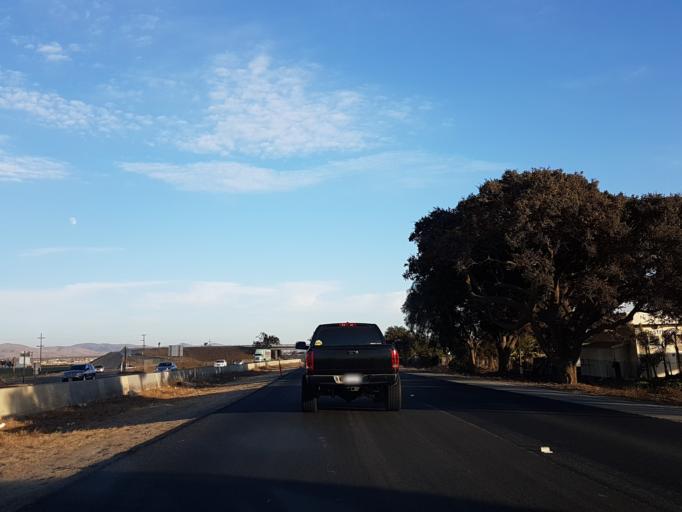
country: US
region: California
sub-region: Monterey County
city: Soledad
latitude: 36.4508
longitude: -121.3657
